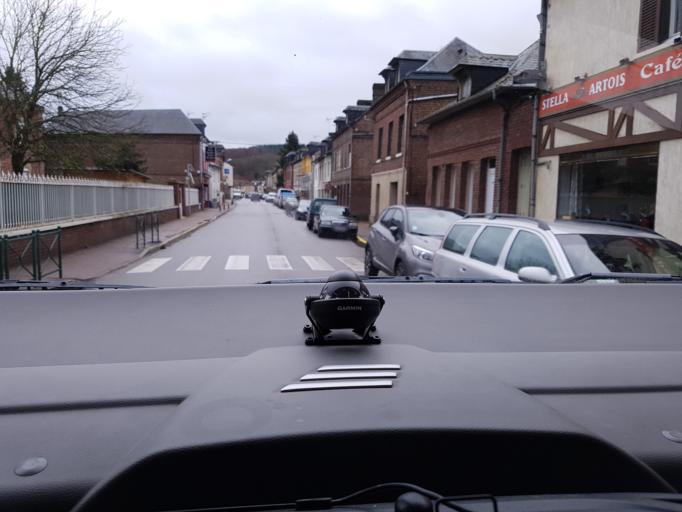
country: FR
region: Haute-Normandie
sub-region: Departement de l'Eure
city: Pont-Saint-Pierre
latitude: 49.3336
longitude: 1.2753
